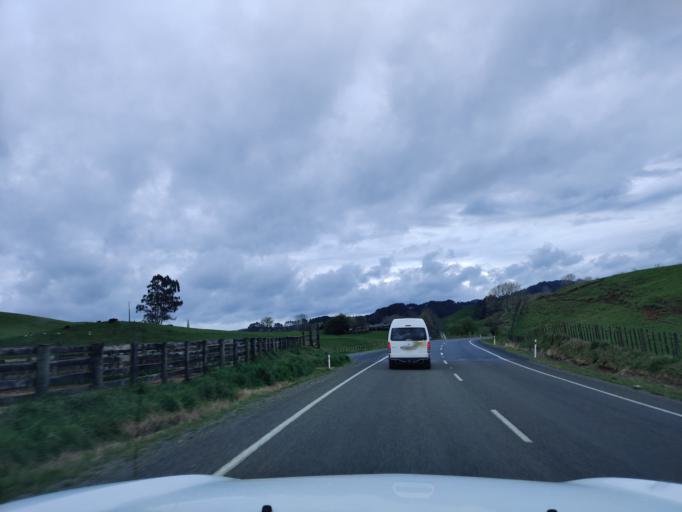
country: NZ
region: Waikato
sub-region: Otorohanga District
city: Otorohanga
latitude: -38.4542
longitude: 175.1644
